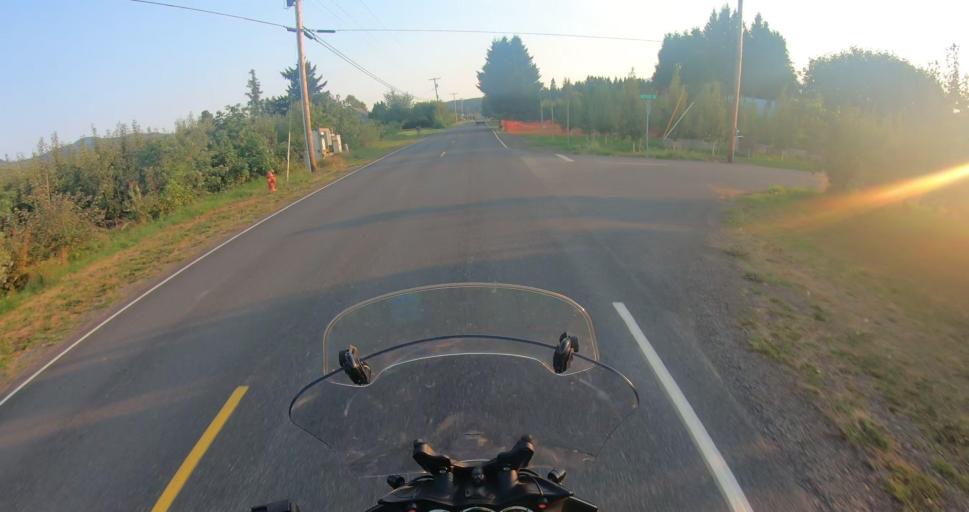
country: US
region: Oregon
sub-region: Hood River County
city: Odell
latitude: 45.5011
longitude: -121.5968
